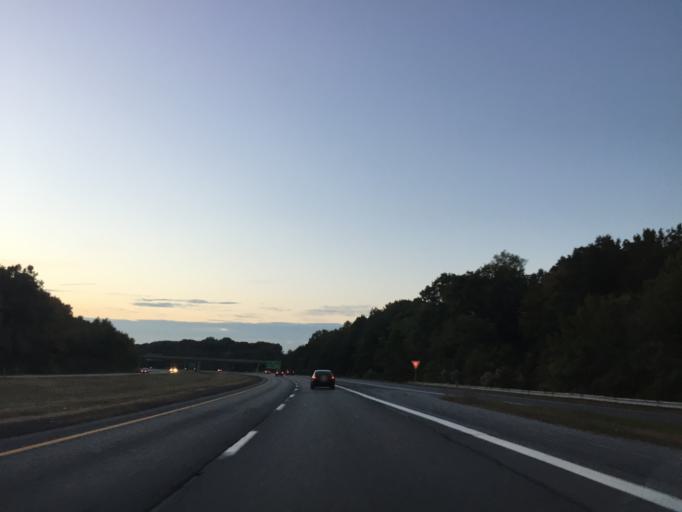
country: US
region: Maryland
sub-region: Baltimore County
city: Essex
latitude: 39.3203
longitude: -76.4591
